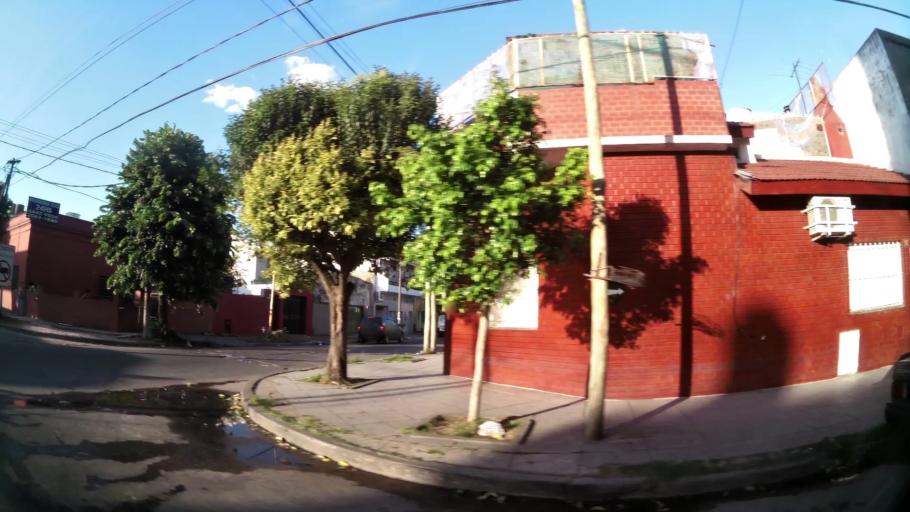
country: AR
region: Buenos Aires F.D.
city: Villa Lugano
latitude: -34.6903
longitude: -58.4846
